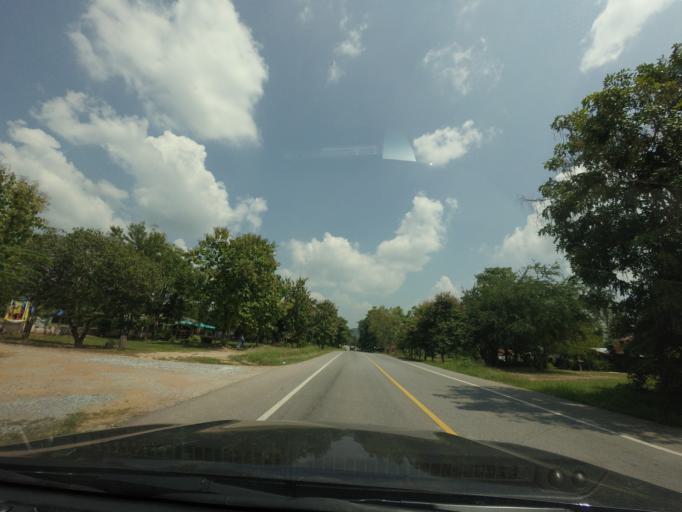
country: TH
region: Phitsanulok
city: Chat Trakan
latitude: 17.2993
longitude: 100.4211
